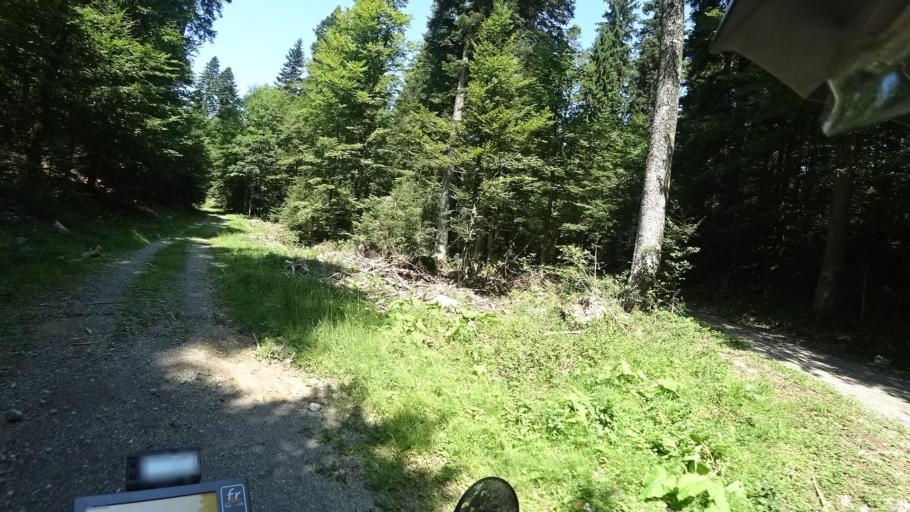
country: HR
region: Primorsko-Goranska
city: Bribir
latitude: 45.2613
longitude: 14.8751
